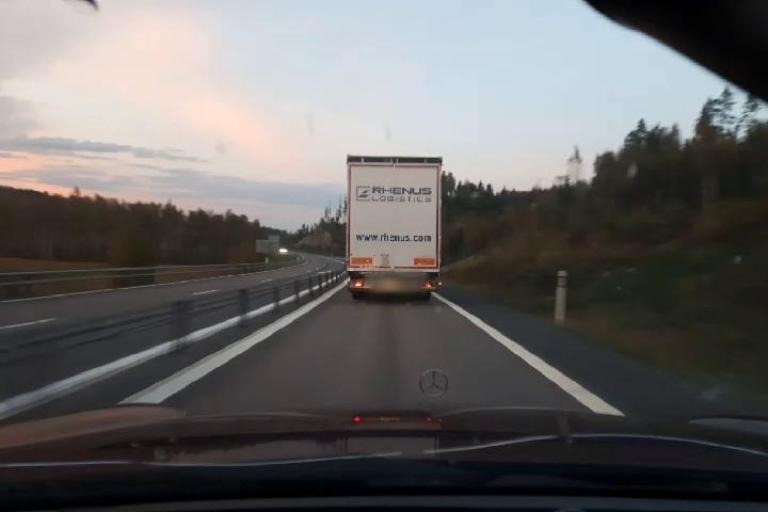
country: SE
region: Vaesternorrland
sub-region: Haernoesands Kommun
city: Haernoesand
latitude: 62.8155
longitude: 17.9676
